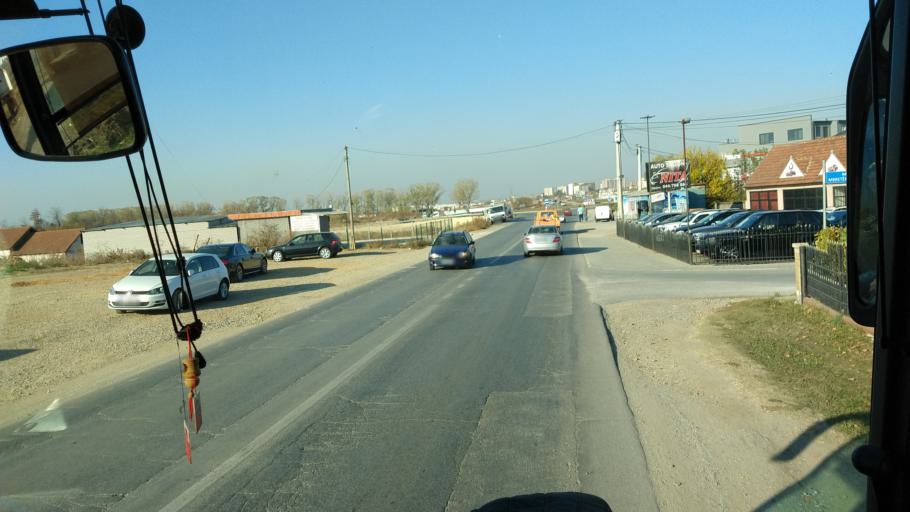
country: XK
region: Pristina
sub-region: Lipjan
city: Lipljan
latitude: 42.5096
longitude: 21.1122
